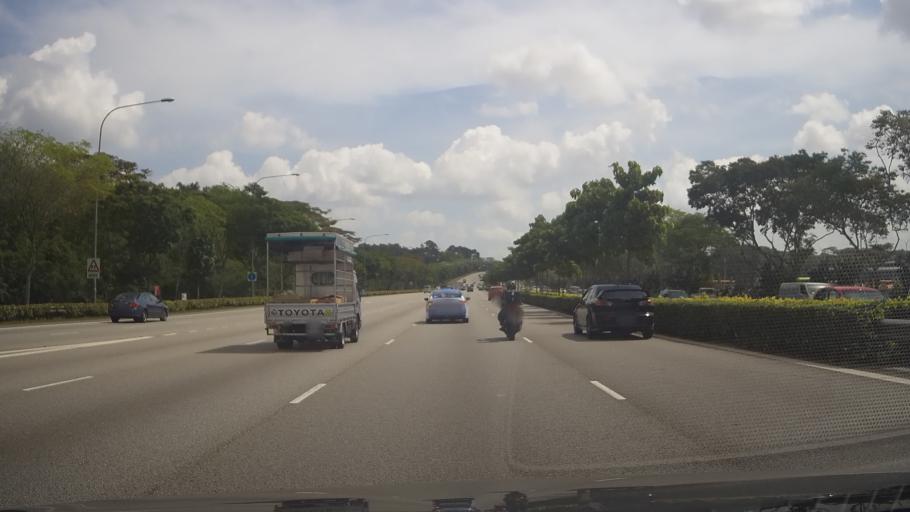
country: MY
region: Johor
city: Kampung Pasir Gudang Baru
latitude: 1.3950
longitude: 103.8362
